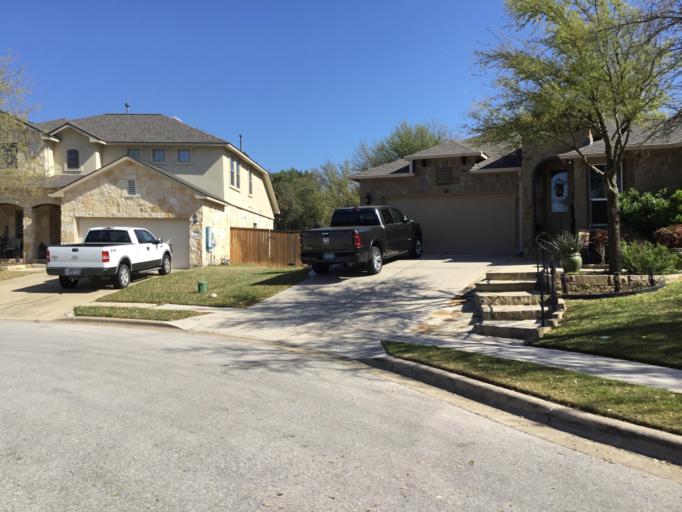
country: US
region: Texas
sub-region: Williamson County
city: Brushy Creek
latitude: 30.5729
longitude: -97.7755
